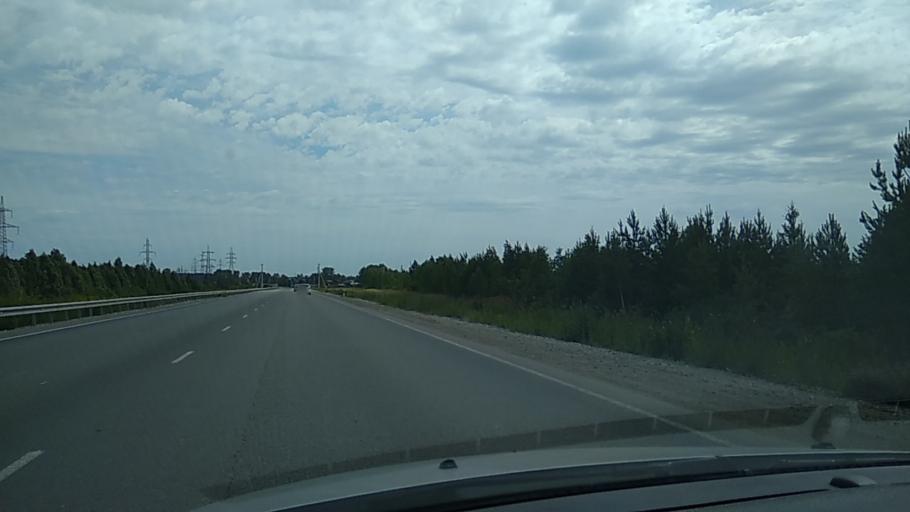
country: RU
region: Sverdlovsk
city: Verkhnyaya Pyshma
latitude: 56.9510
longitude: 60.5897
